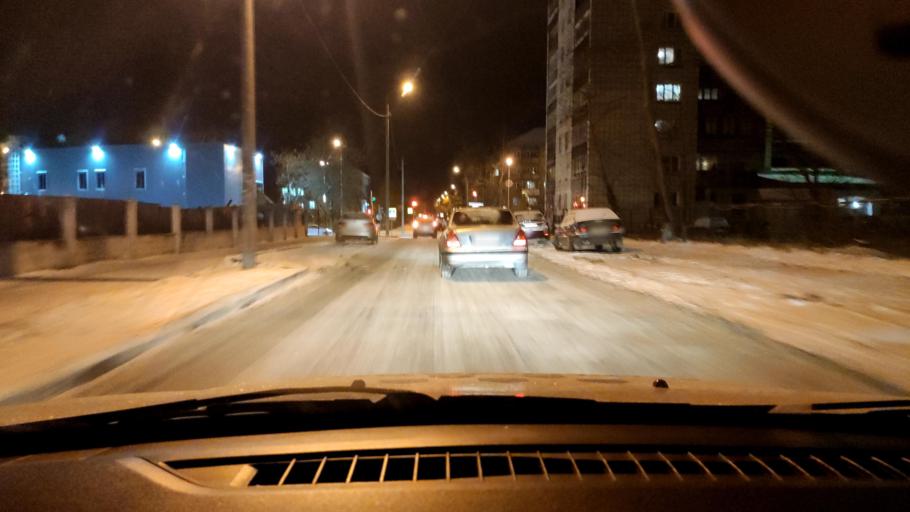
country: RU
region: Perm
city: Kultayevo
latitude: 58.0086
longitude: 55.9547
